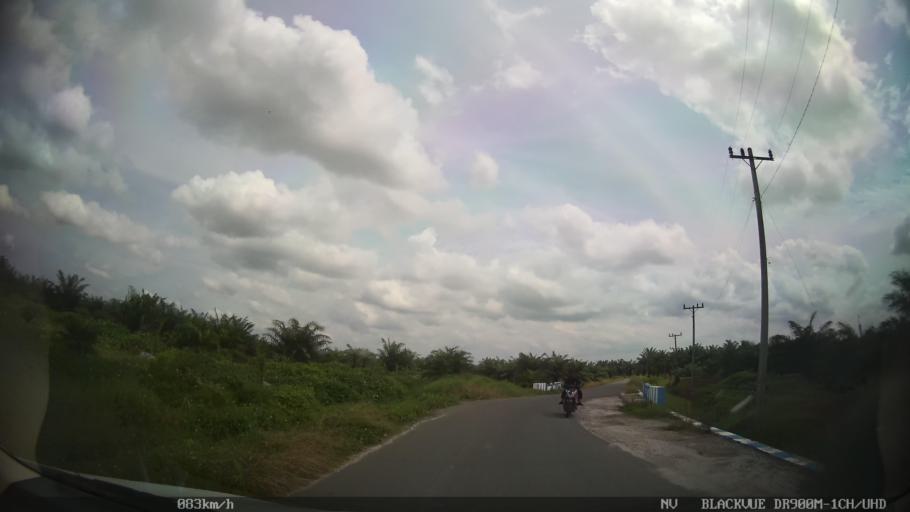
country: ID
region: North Sumatra
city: Percut
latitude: 3.5892
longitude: 98.8410
